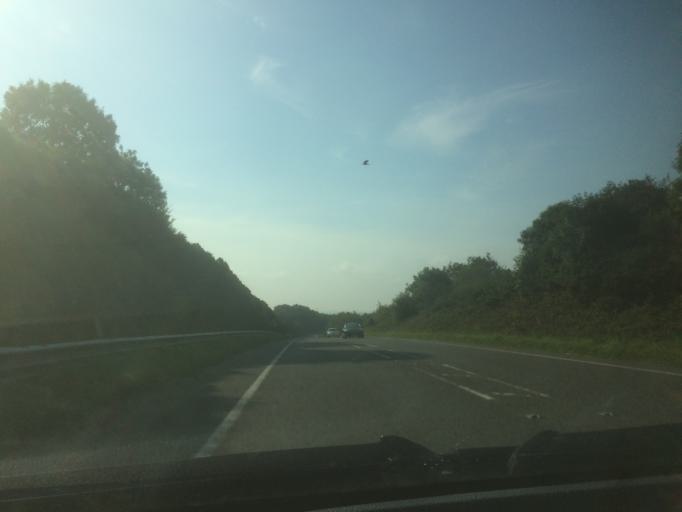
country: GB
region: England
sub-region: Cornwall
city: Pillaton
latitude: 50.4577
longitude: -4.2591
